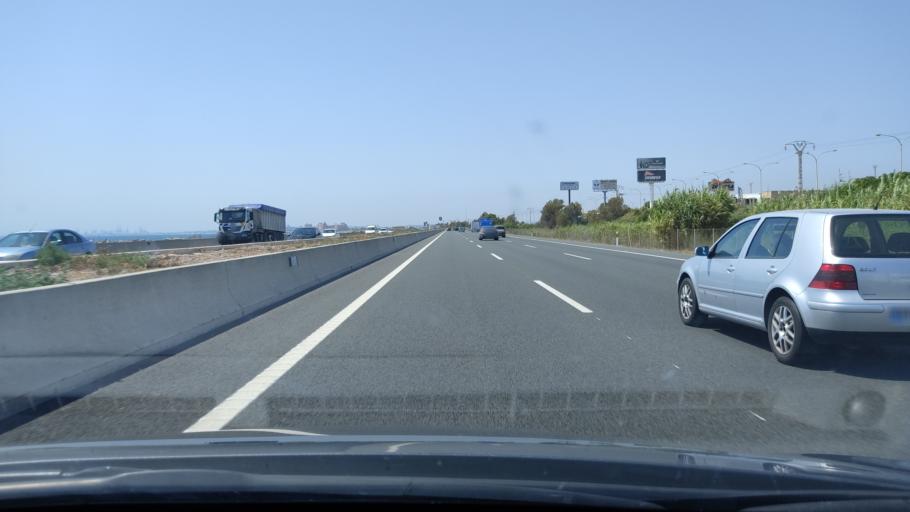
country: ES
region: Valencia
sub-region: Provincia de Valencia
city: Albuixech
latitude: 39.5393
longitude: -0.3053
